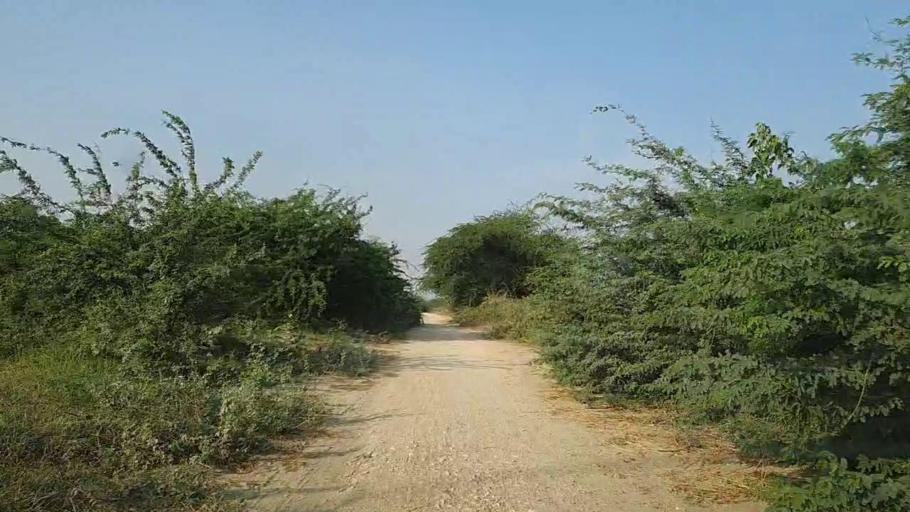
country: PK
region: Sindh
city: Mirpur Sakro
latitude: 24.5981
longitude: 67.6491
